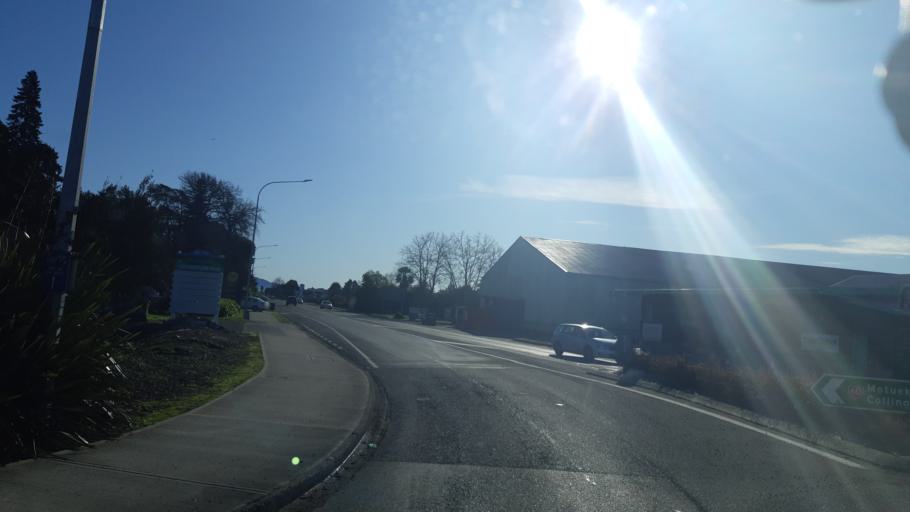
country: NZ
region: Tasman
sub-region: Tasman District
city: Motueka
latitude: -41.1330
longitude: 173.0098
